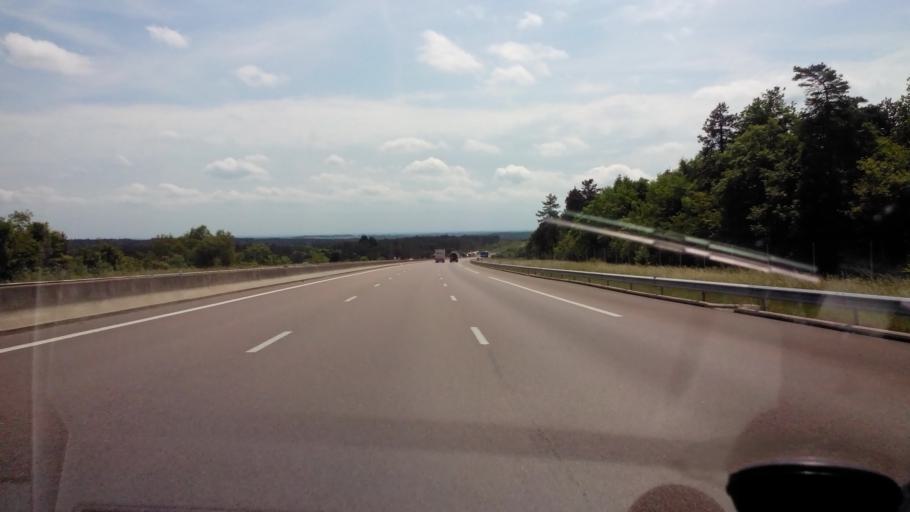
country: FR
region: Bourgogne
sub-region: Departement de la Cote-d'Or
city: Selongey
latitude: 47.6073
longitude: 5.1936
